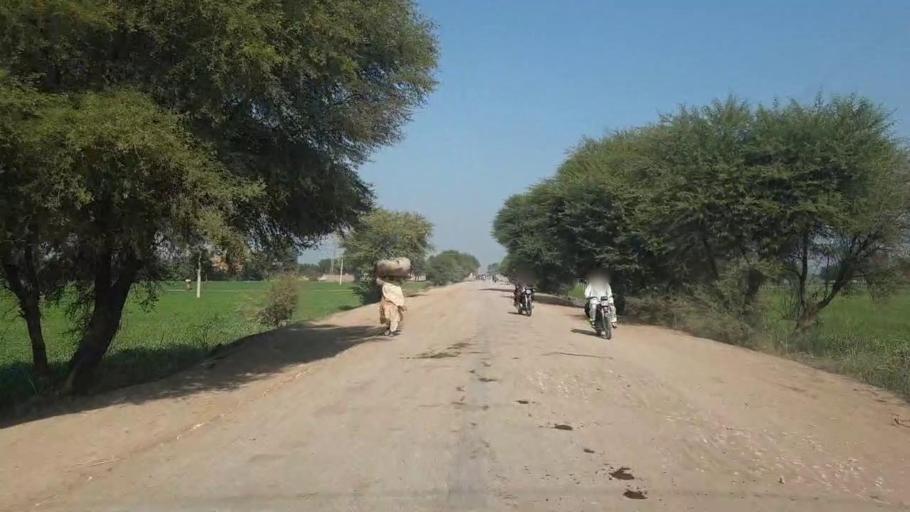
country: PK
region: Sindh
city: Sakrand
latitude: 26.0496
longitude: 68.4031
